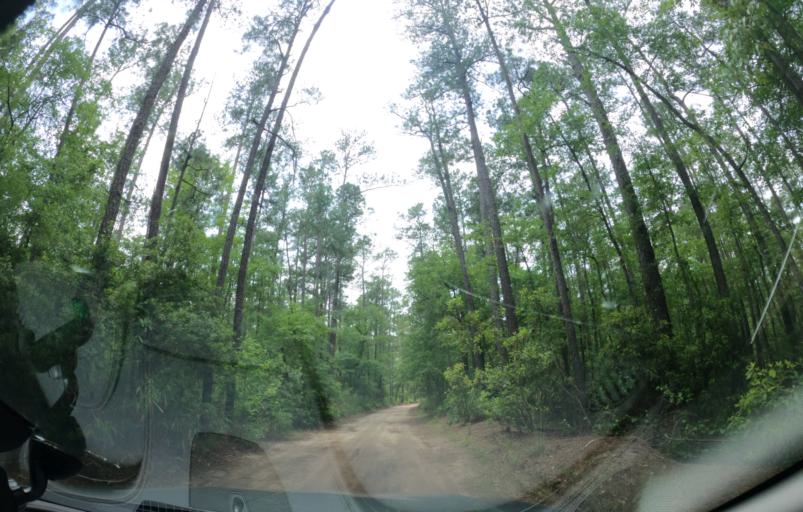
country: US
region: South Carolina
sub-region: Barnwell County
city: Williston
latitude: 33.5512
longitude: -81.4871
